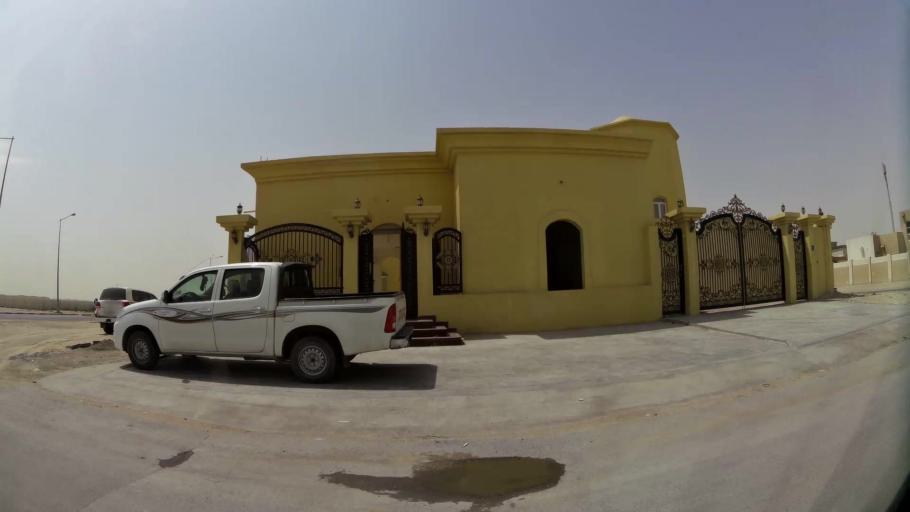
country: QA
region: Baladiyat ar Rayyan
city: Ar Rayyan
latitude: 25.2277
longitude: 51.4142
